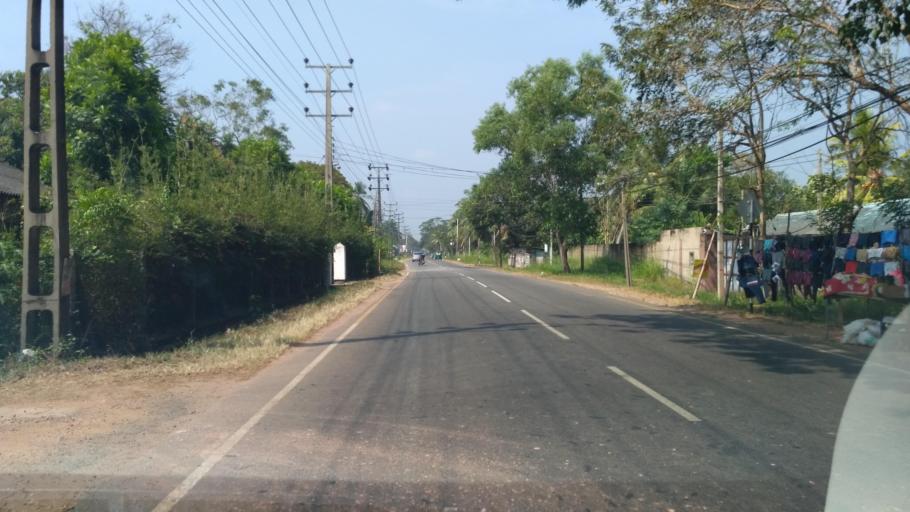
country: LK
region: North Western
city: Kuliyapitiya
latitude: 7.3254
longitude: 79.9867
